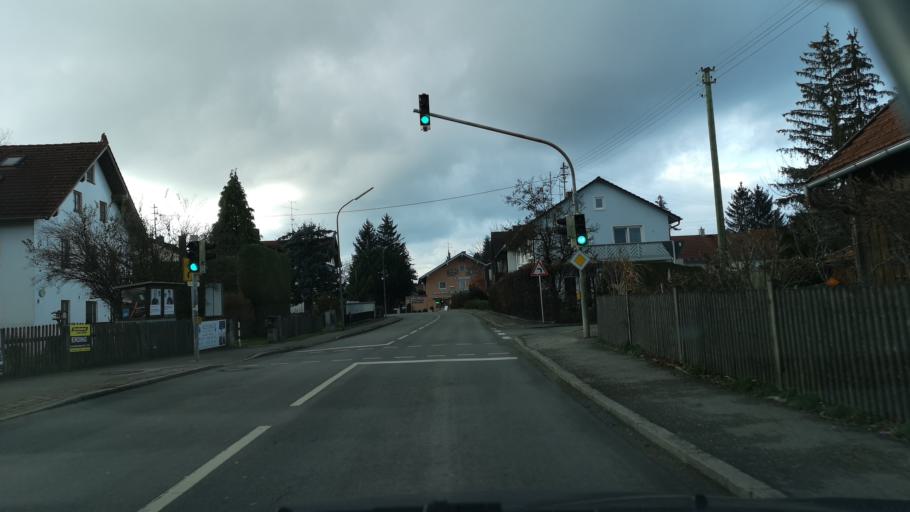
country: DE
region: Bavaria
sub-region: Upper Bavaria
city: Kirchheim bei Muenchen
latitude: 48.1881
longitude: 11.7762
